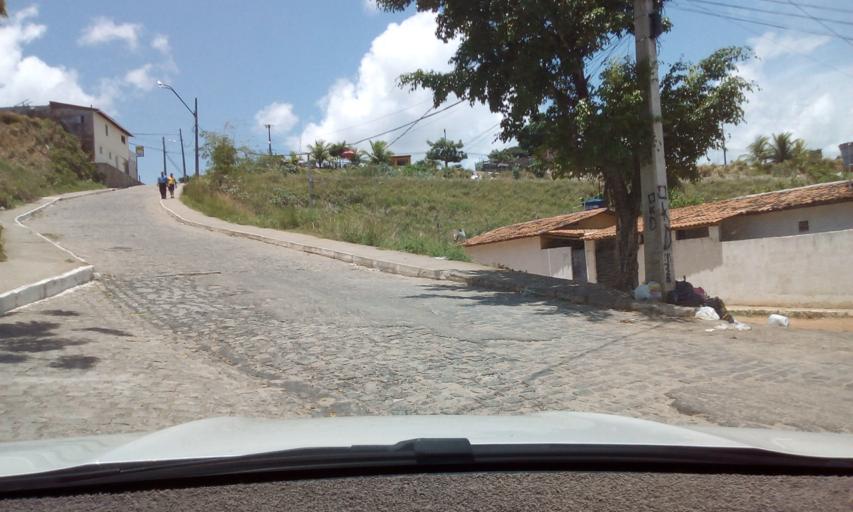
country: BR
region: Paraiba
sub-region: Joao Pessoa
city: Joao Pessoa
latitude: -7.1491
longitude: -34.8288
